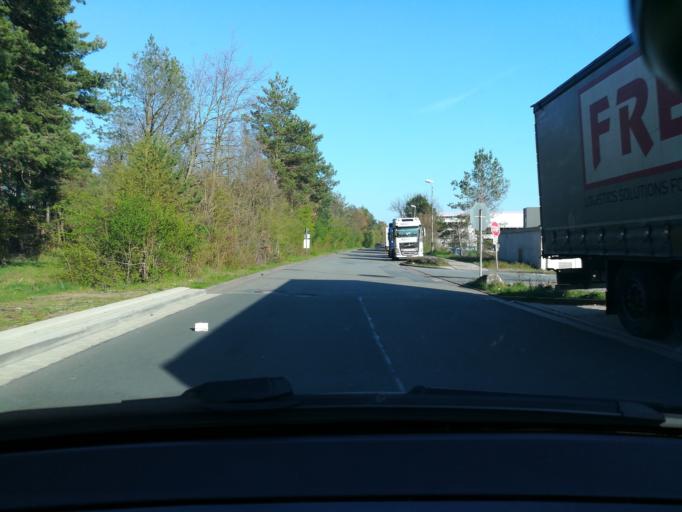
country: DE
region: North Rhine-Westphalia
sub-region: Regierungsbezirk Detmold
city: Verl
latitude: 51.9449
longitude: 8.5633
